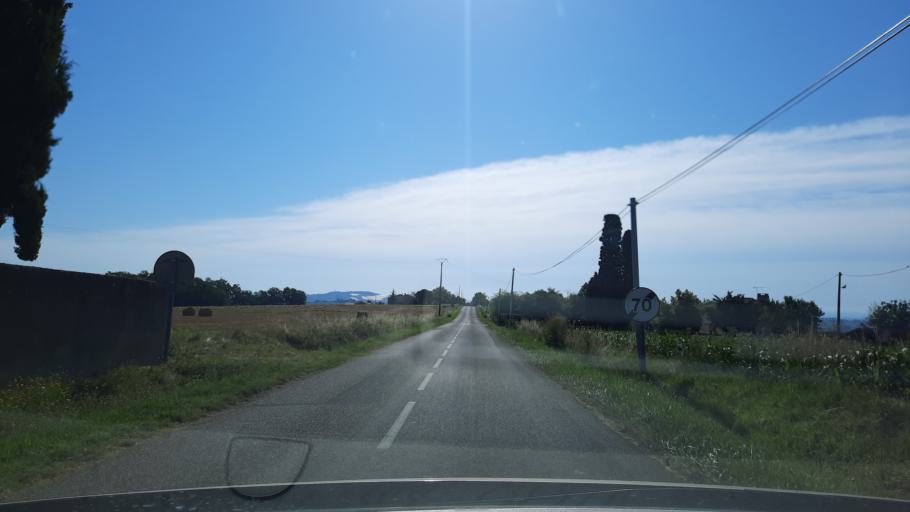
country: FR
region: Midi-Pyrenees
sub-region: Departement du Tarn-et-Garonne
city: Molieres
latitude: 44.2029
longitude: 1.4039
